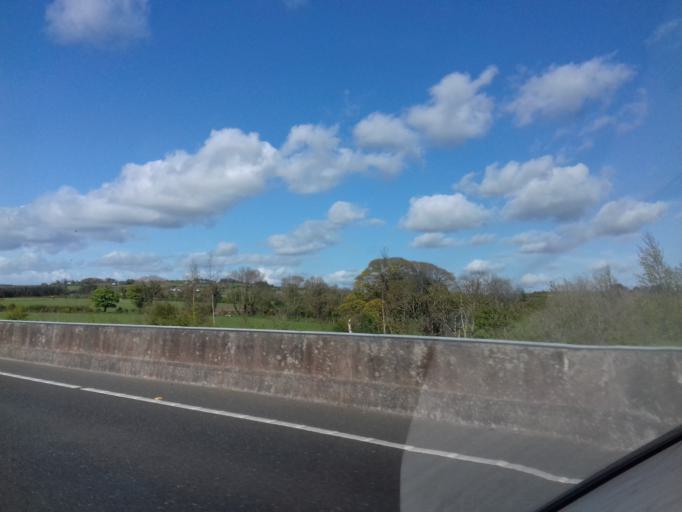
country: IE
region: Leinster
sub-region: Kilkenny
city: Mooncoin
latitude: 52.3589
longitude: -7.1659
